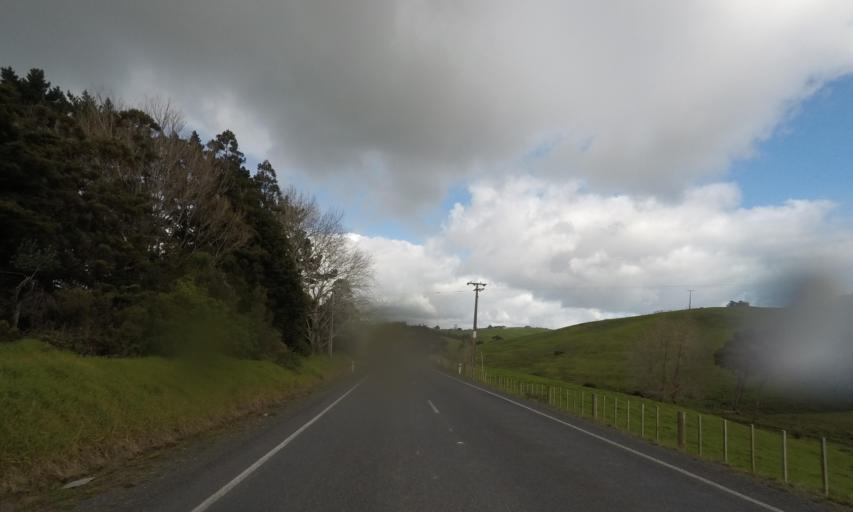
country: NZ
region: Auckland
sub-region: Auckland
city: Wellsford
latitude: -36.1704
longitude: 174.5829
